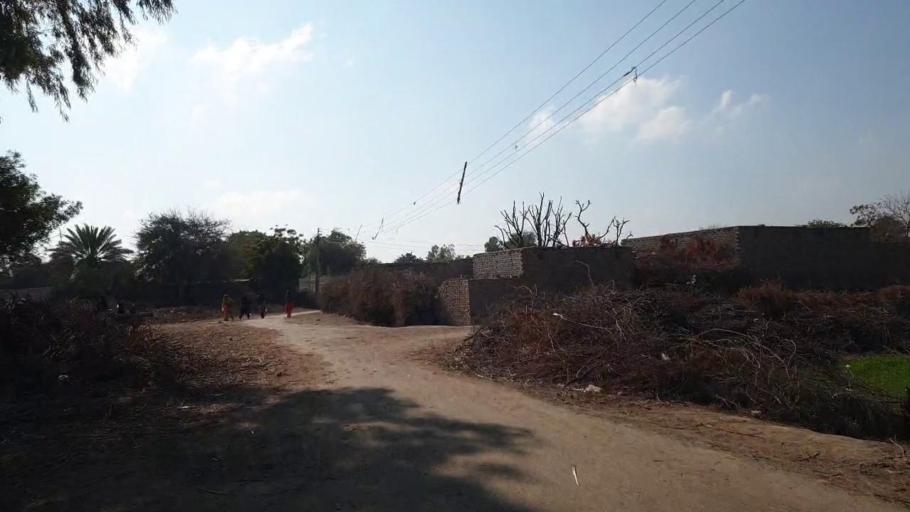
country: PK
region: Sindh
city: Shahpur Chakar
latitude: 26.0525
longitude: 68.5842
